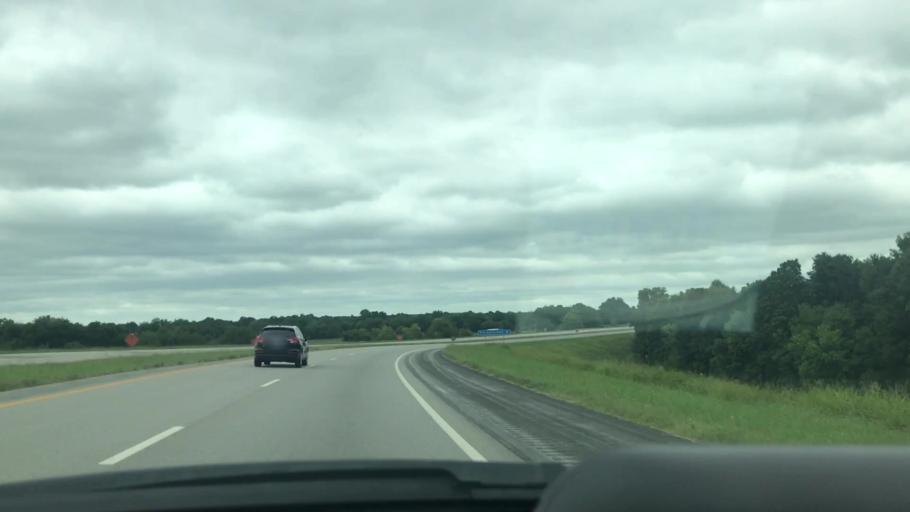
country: US
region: Oklahoma
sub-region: Mayes County
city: Pryor
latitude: 36.3744
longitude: -95.2958
